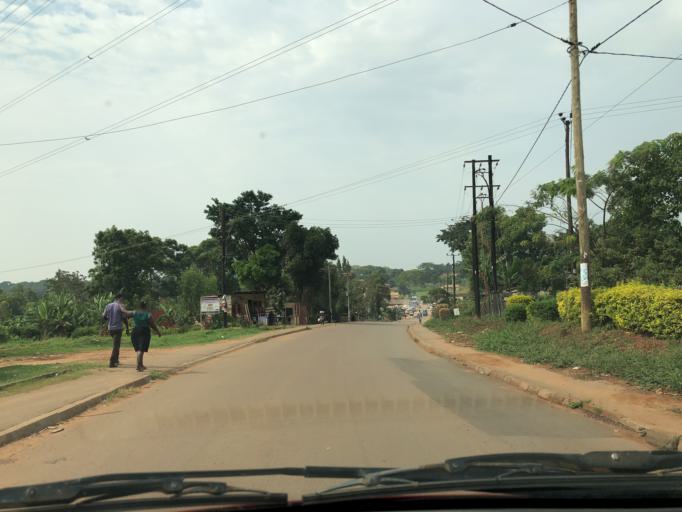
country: UG
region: Central Region
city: Kampala Central Division
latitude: 0.4020
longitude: 32.5895
